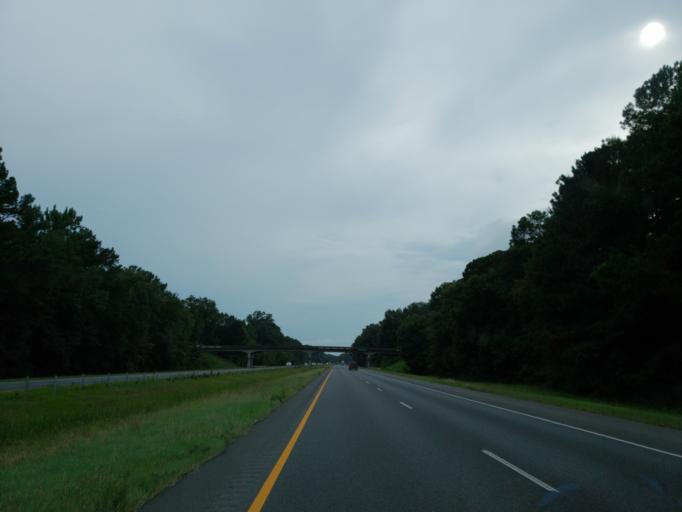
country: US
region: Alabama
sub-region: Greene County
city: Eutaw
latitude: 32.8302
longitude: -87.9779
